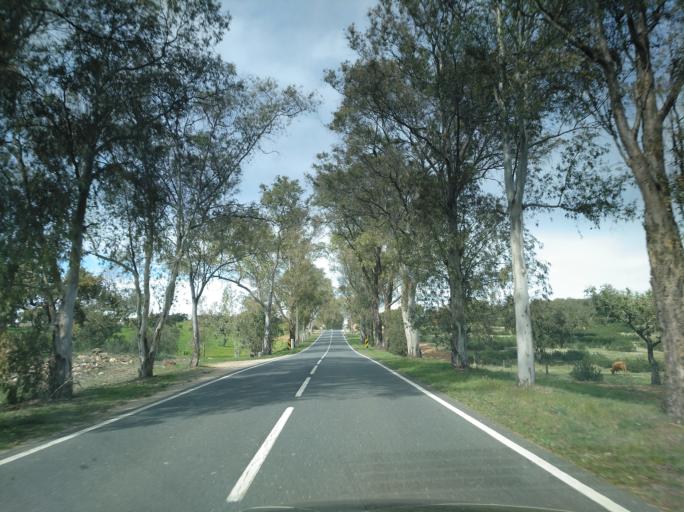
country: PT
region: Beja
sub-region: Mertola
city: Mertola
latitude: 37.7253
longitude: -7.7641
